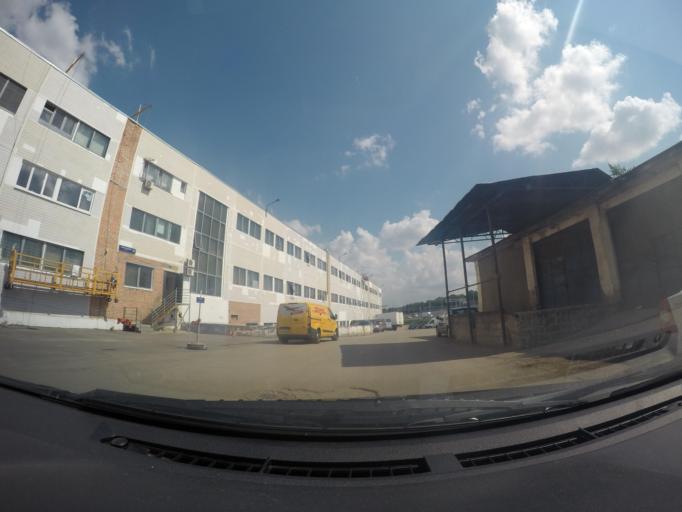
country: RU
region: Moscow
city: Novovladykino
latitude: 55.8487
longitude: 37.5998
